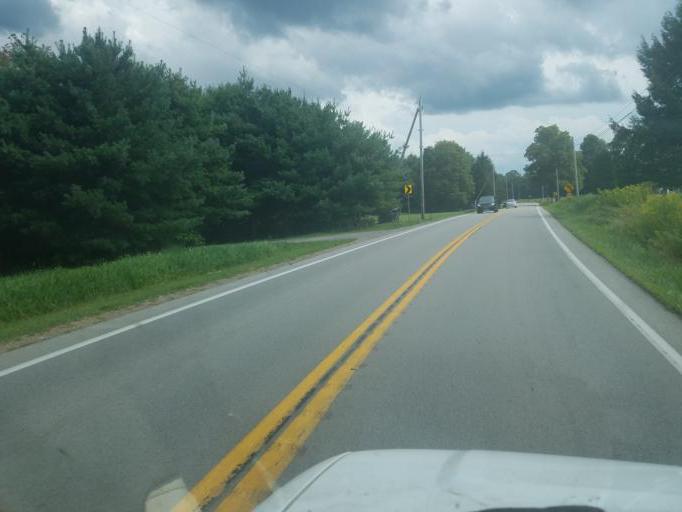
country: US
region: Pennsylvania
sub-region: Crawford County
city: Conneaut Lakeshore
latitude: 41.5800
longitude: -80.2943
